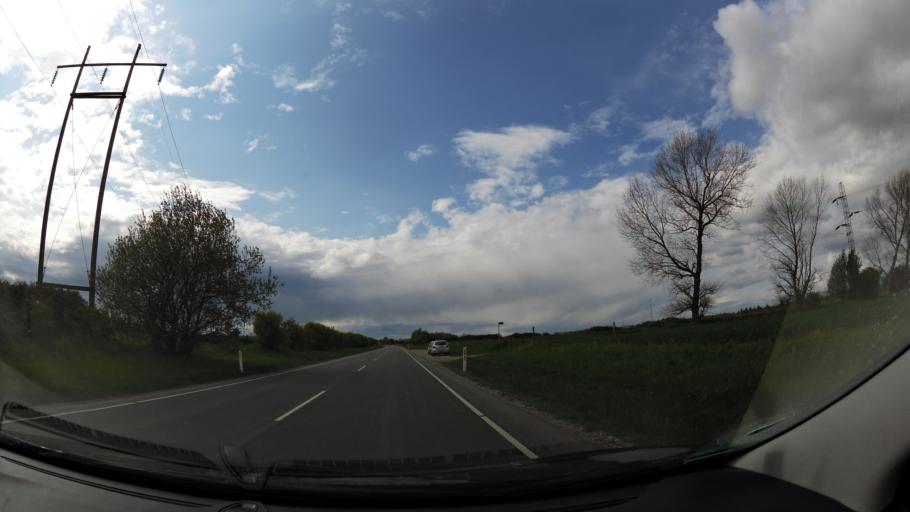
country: DK
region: South Denmark
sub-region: Nyborg Kommune
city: Nyborg
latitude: 55.3181
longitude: 10.7469
